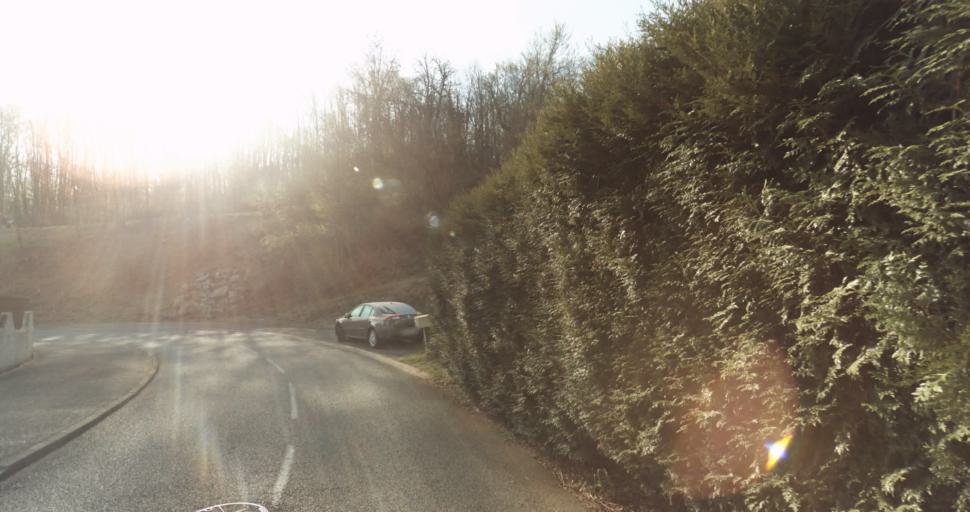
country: FR
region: Rhone-Alpes
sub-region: Departement de la Loire
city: Saint-Jean-Bonnefonds
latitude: 45.4443
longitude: 4.4428
